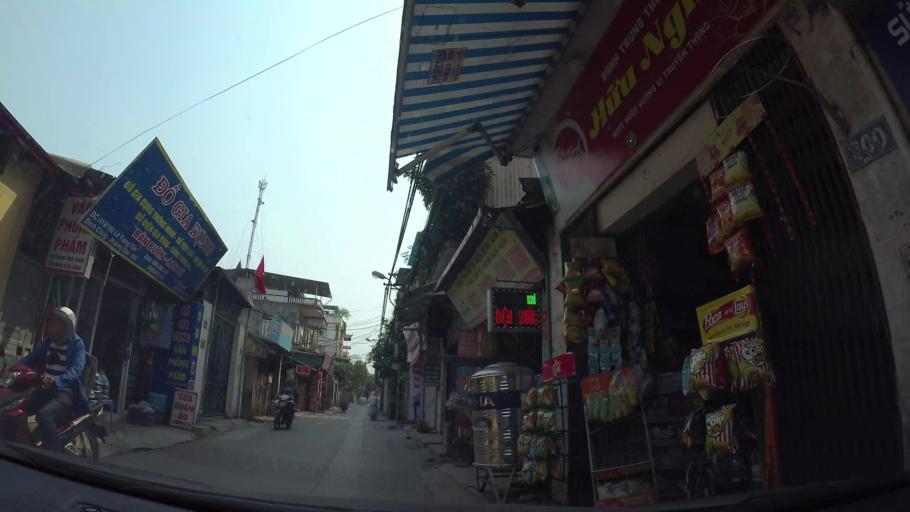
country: VN
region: Ha Noi
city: Thanh Xuan
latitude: 20.9861
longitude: 105.8246
